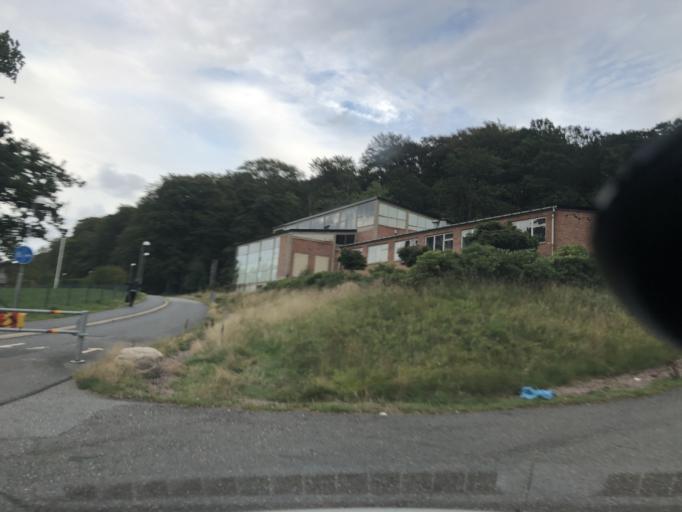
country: SE
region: Vaestra Goetaland
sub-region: Goteborg
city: Goeteborg
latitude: 57.7492
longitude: 11.9543
